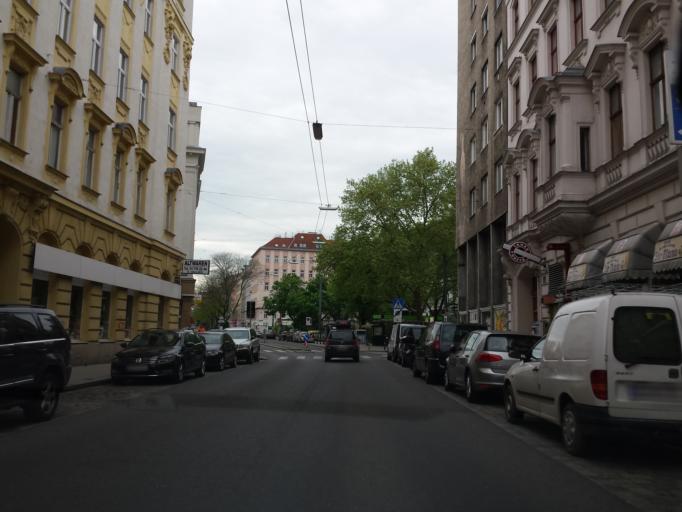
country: AT
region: Vienna
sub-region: Wien Stadt
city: Vienna
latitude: 48.1982
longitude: 16.4007
